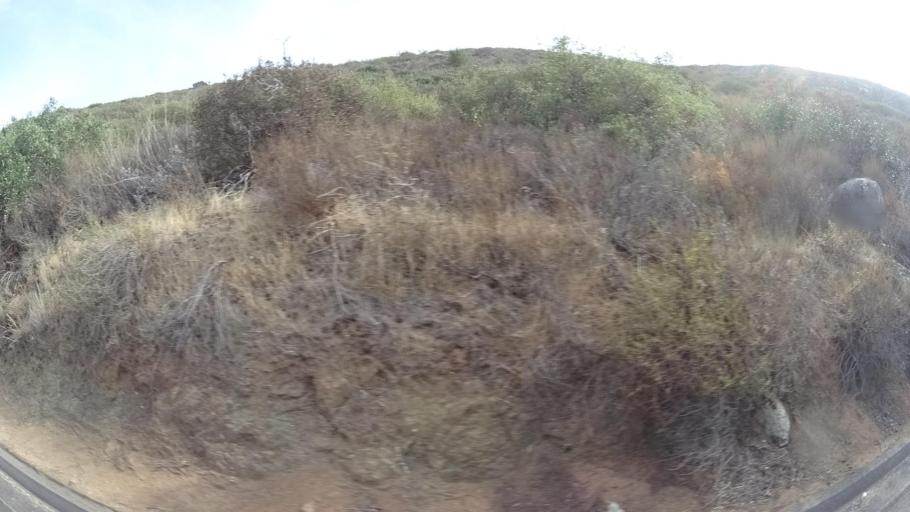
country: US
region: California
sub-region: San Diego County
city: San Pasqual
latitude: 33.0865
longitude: -116.9061
